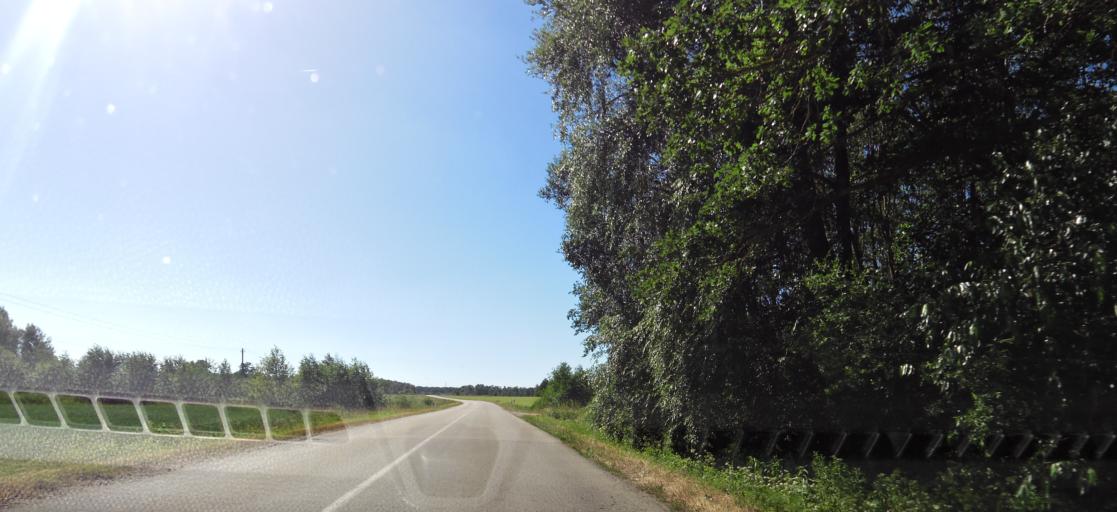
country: LT
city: Vabalninkas
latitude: 56.0027
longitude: 24.6490
